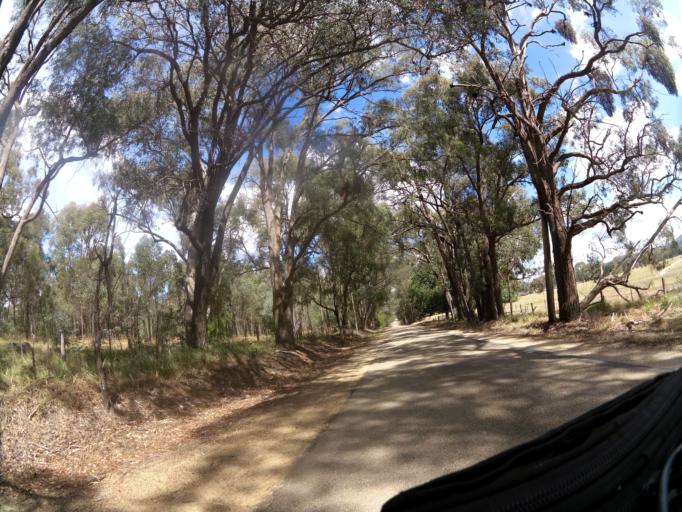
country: AU
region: Victoria
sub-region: Benalla
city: Benalla
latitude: -36.7747
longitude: 145.9742
